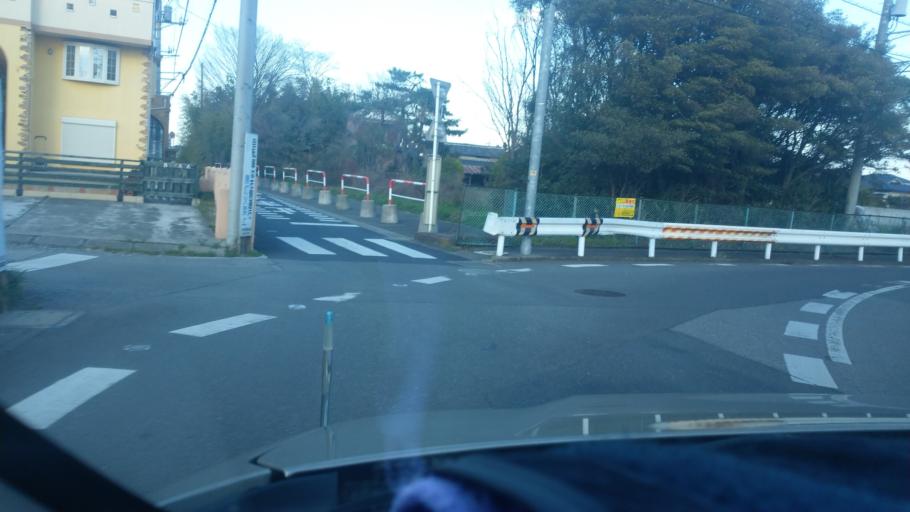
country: JP
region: Saitama
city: Yono
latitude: 35.8903
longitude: 139.5968
